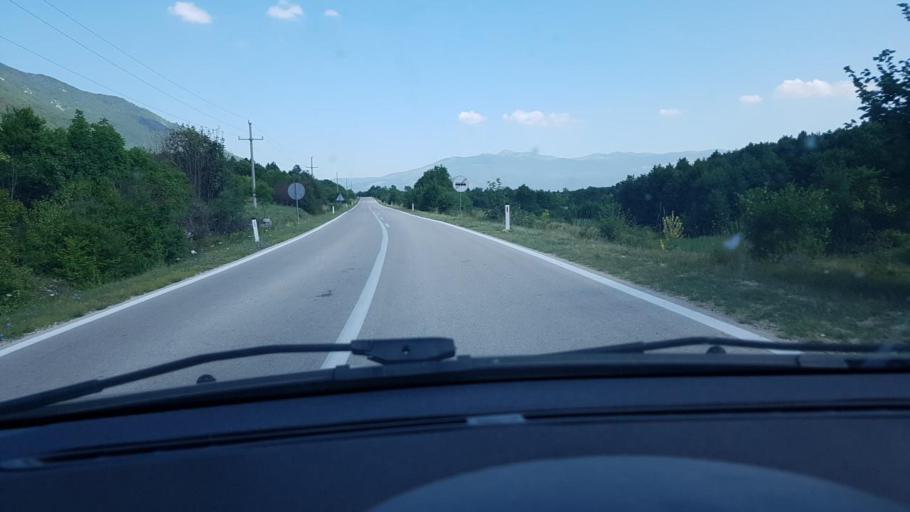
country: BA
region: Federation of Bosnia and Herzegovina
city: Glamoc
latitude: 44.0126
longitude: 16.6034
